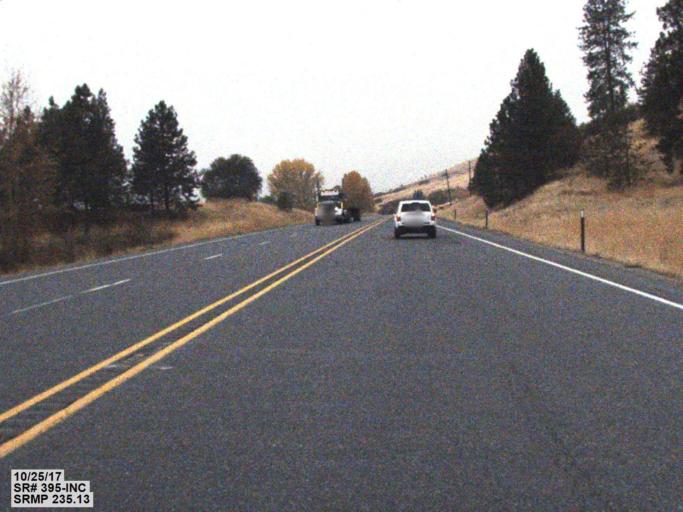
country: US
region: Washington
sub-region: Stevens County
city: Kettle Falls
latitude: 48.5929
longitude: -117.9978
